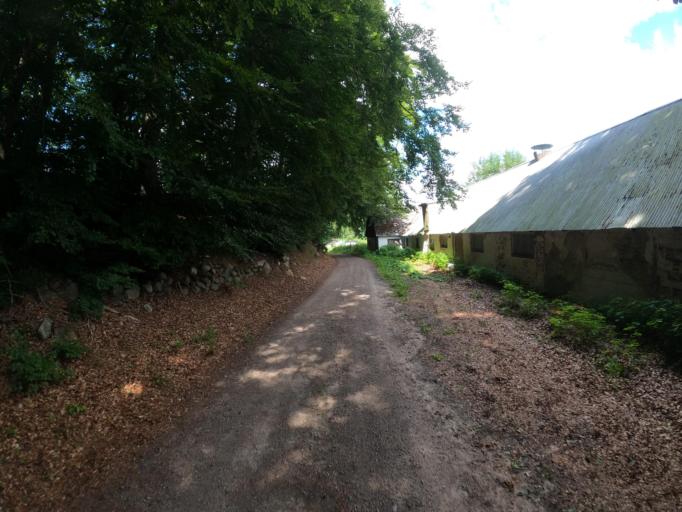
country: SE
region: Skane
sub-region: Lunds Kommun
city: Veberod
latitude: 55.5930
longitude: 13.4833
